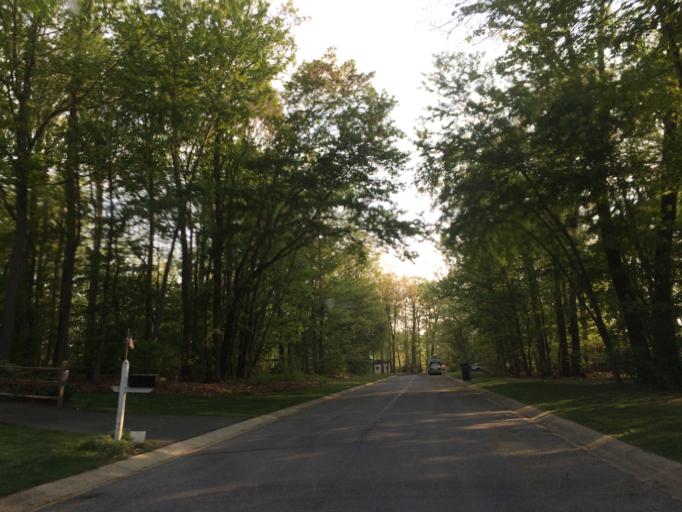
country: US
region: Maryland
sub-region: Carroll County
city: Sykesville
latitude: 39.3987
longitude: -77.0357
